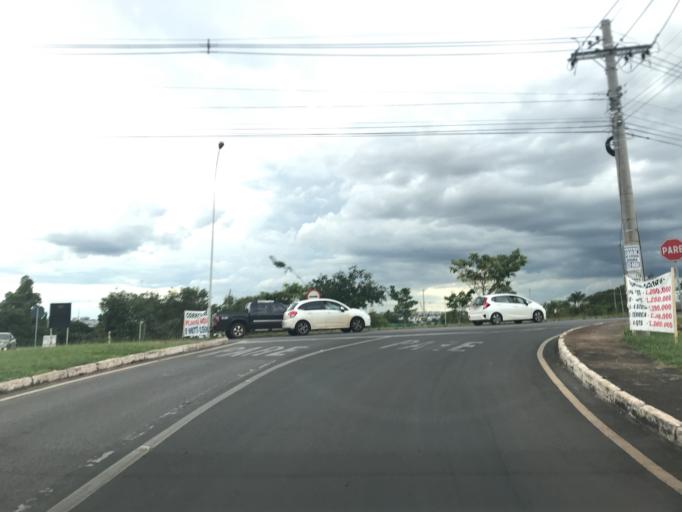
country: BR
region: Federal District
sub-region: Brasilia
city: Brasilia
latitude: -15.7220
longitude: -47.8814
